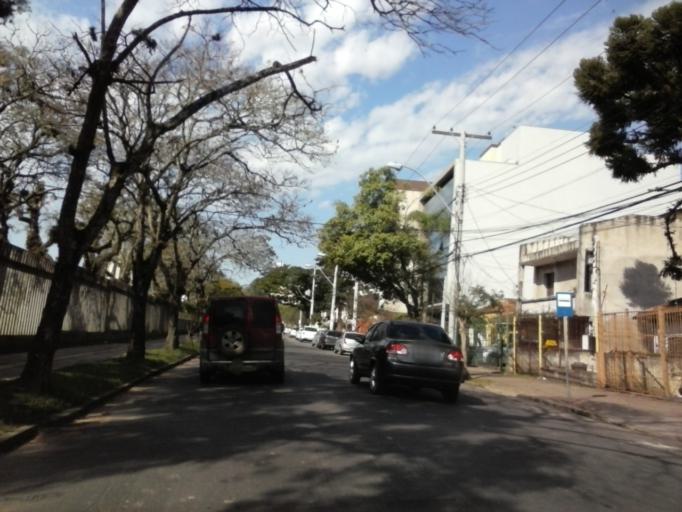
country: BR
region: Rio Grande do Sul
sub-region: Porto Alegre
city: Porto Alegre
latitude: -30.0512
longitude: -51.1835
